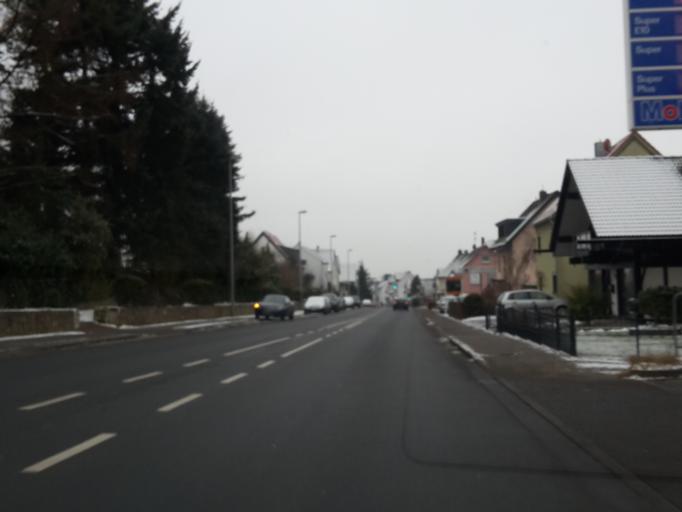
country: DE
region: Hesse
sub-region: Regierungsbezirk Darmstadt
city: Glashutten
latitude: 50.2205
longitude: 8.4051
